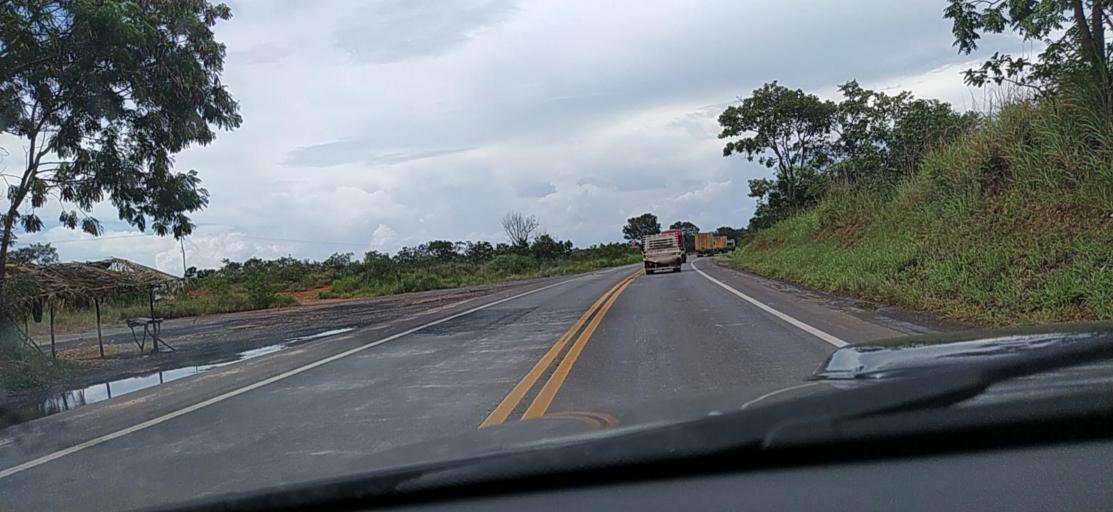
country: BR
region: Minas Gerais
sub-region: Montes Claros
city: Montes Claros
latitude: -16.8484
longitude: -43.8519
